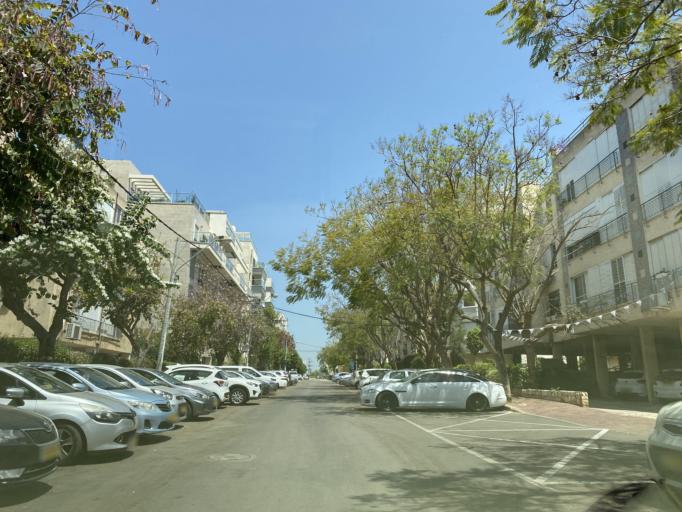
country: IL
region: Central District
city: Ra'anana
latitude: 32.1763
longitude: 34.8786
